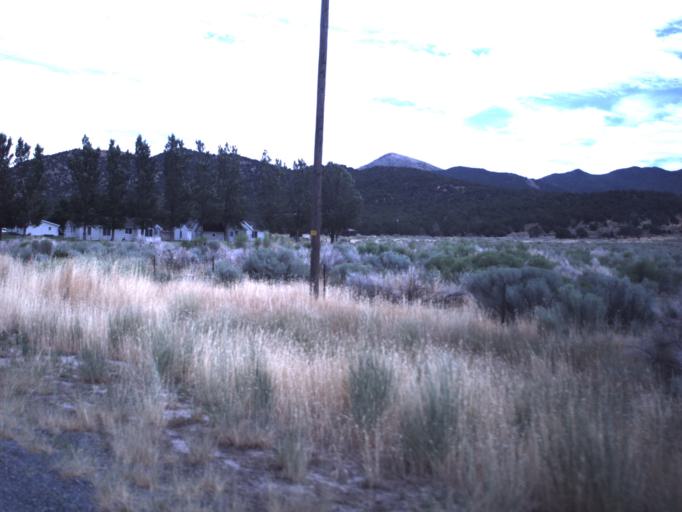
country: US
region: Utah
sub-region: Beaver County
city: Beaver
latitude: 38.5983
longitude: -112.5814
